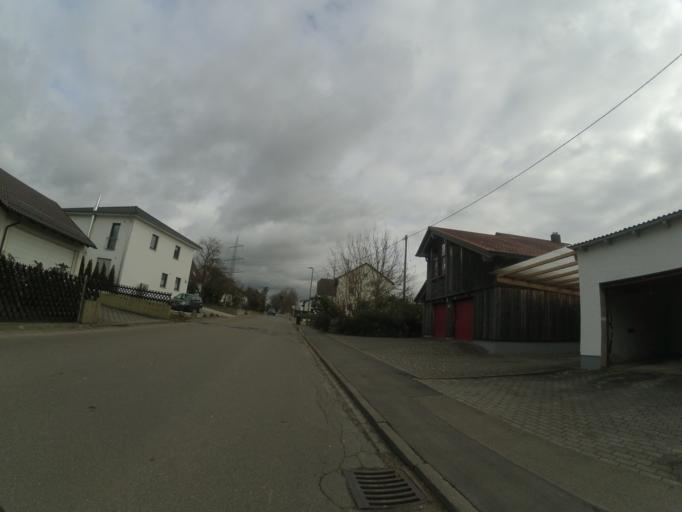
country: DE
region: Bavaria
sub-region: Swabia
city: Bellenberg
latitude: 48.2546
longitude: 10.1223
